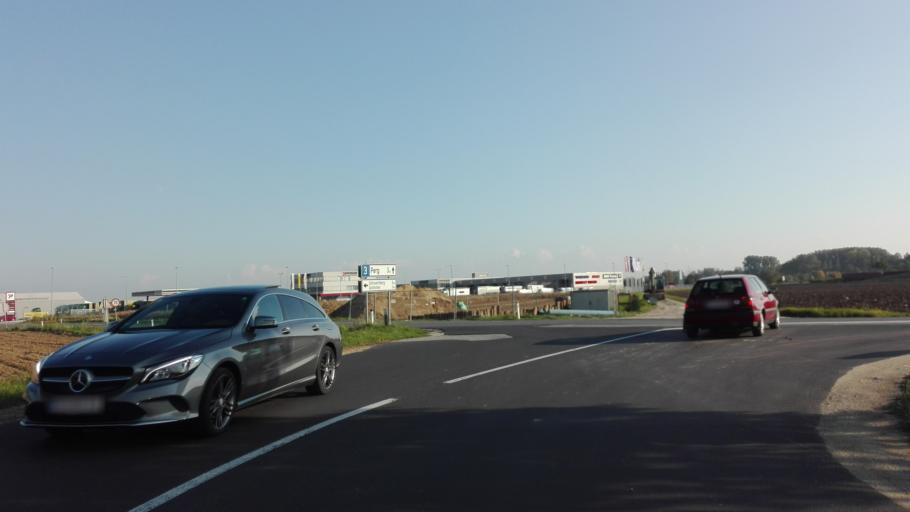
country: AT
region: Upper Austria
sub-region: Politischer Bezirk Perg
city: Perg
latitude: 48.2535
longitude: 14.5940
